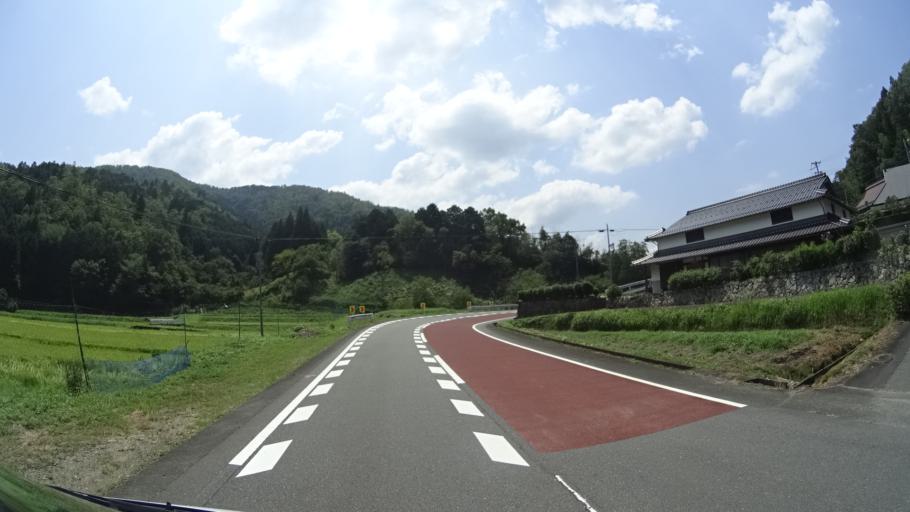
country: JP
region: Kyoto
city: Ayabe
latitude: 35.2135
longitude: 135.2077
